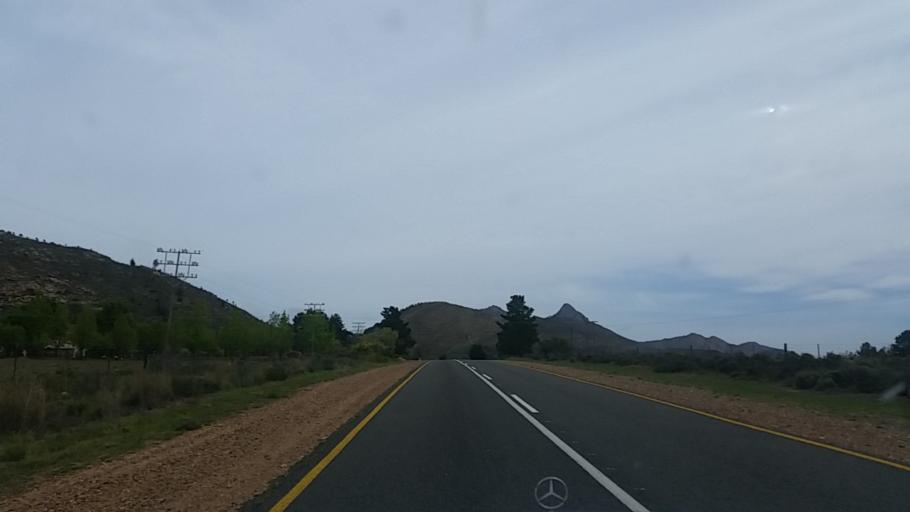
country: ZA
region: Western Cape
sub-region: Eden District Municipality
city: George
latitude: -33.8323
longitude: 22.4557
